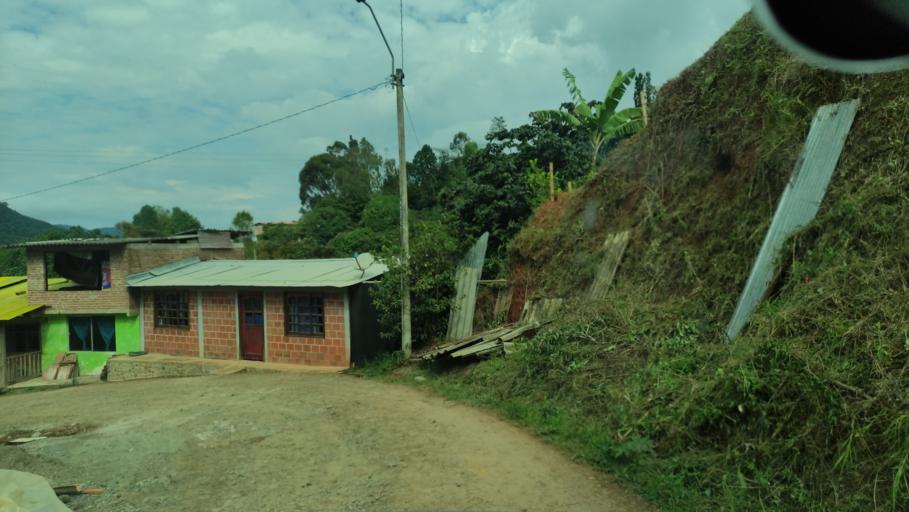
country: CO
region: Valle del Cauca
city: Cali
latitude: 3.4534
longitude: -76.6339
